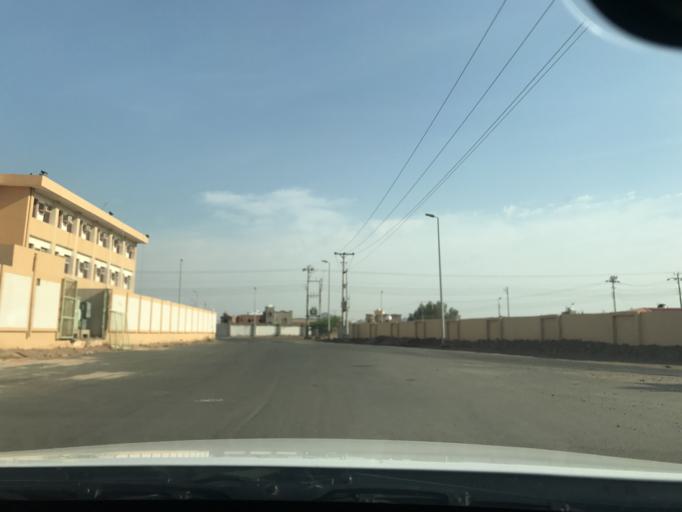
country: SA
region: Makkah
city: Al Jumum
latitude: 21.4515
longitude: 39.5391
